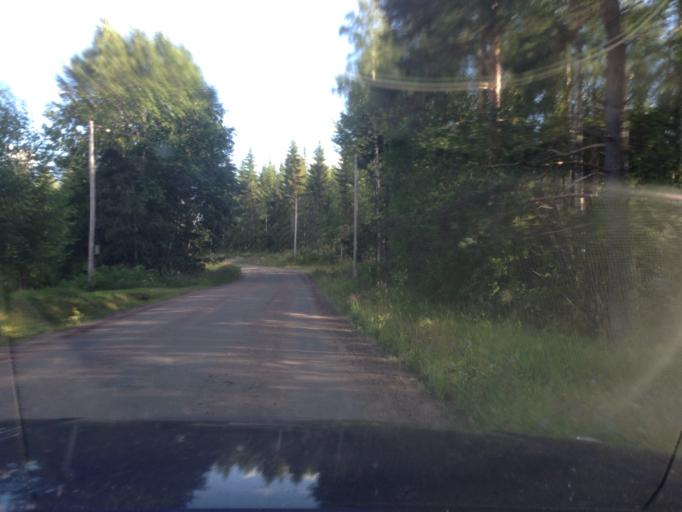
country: SE
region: Dalarna
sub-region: Ludvika Kommun
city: Abborrberget
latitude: 60.2678
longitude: 14.7348
